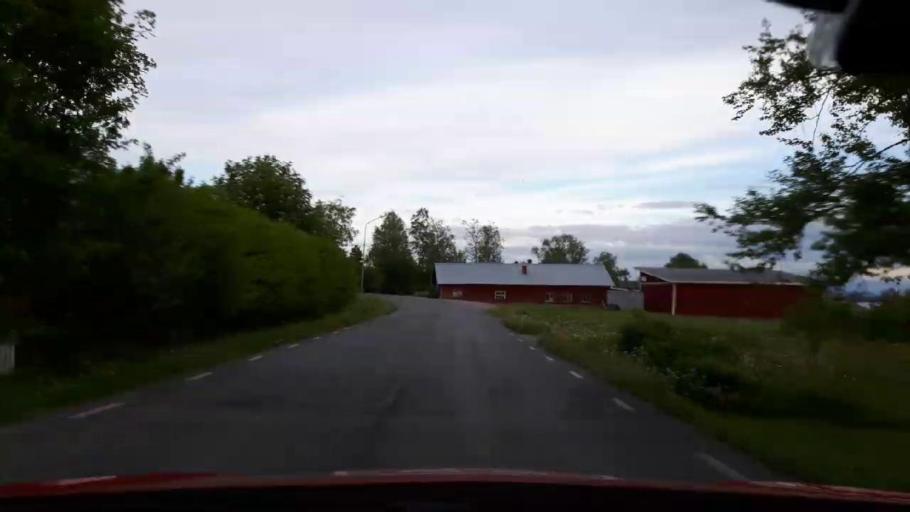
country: SE
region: Jaemtland
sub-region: OEstersunds Kommun
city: Ostersund
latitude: 63.0422
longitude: 14.4575
